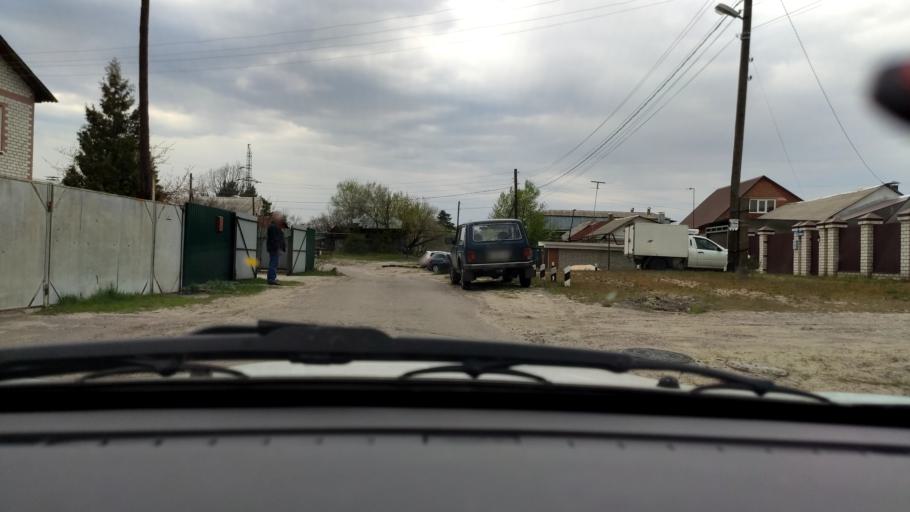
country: RU
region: Voronezj
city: Somovo
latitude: 51.7349
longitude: 39.3343
